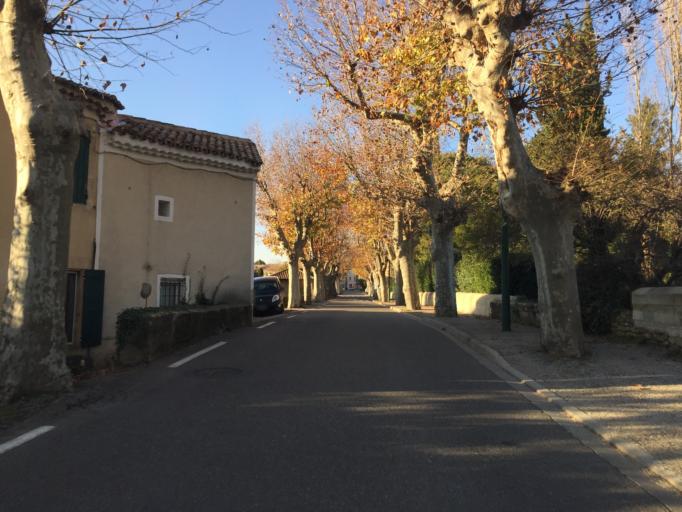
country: FR
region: Provence-Alpes-Cote d'Azur
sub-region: Departement du Vaucluse
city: Serignan-du-Comtat
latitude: 44.1867
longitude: 4.8467
